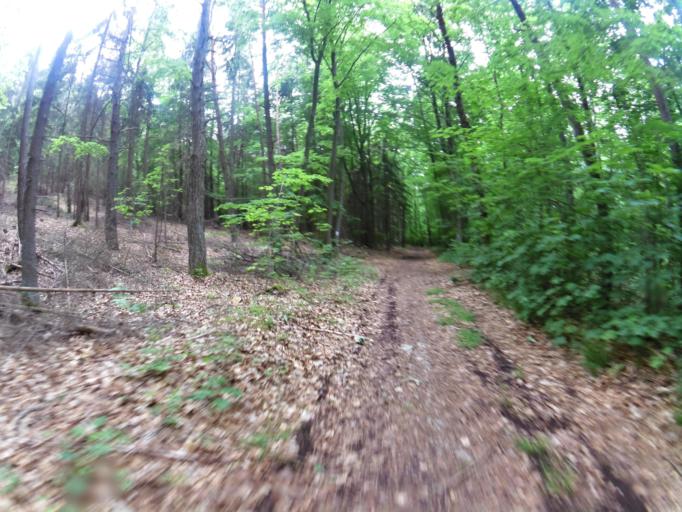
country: DE
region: Bavaria
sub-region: Regierungsbezirk Unterfranken
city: Thungersheim
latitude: 49.8771
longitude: 9.8688
